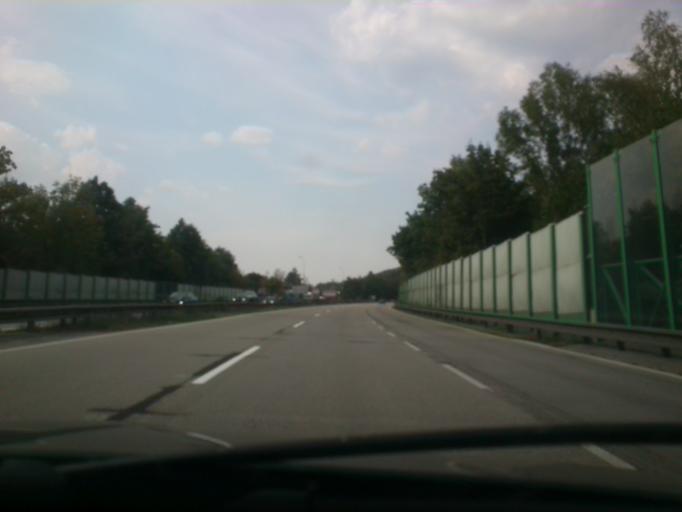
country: CZ
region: Central Bohemia
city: Ondrejov
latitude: 49.8766
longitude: 14.7597
